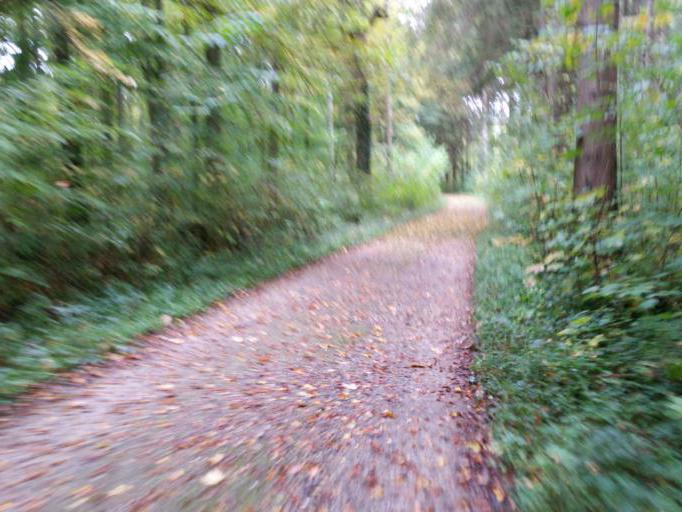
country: CH
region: Thurgau
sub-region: Arbon District
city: Uttwil
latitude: 47.5689
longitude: 9.3446
